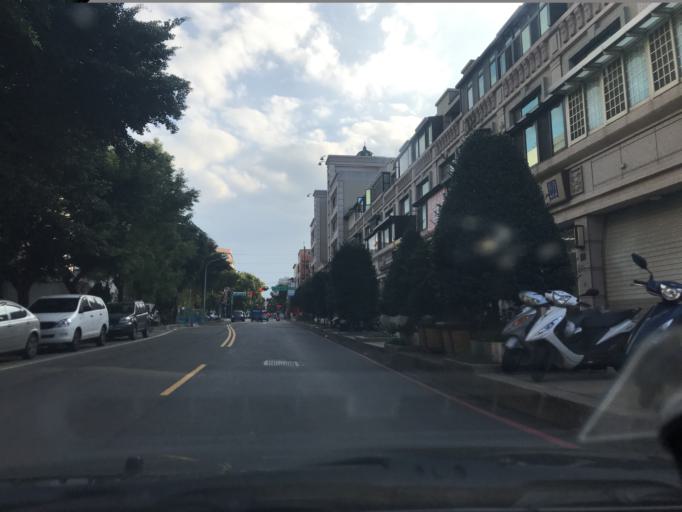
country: TW
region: Taiwan
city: Taoyuan City
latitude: 24.9789
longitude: 121.2346
